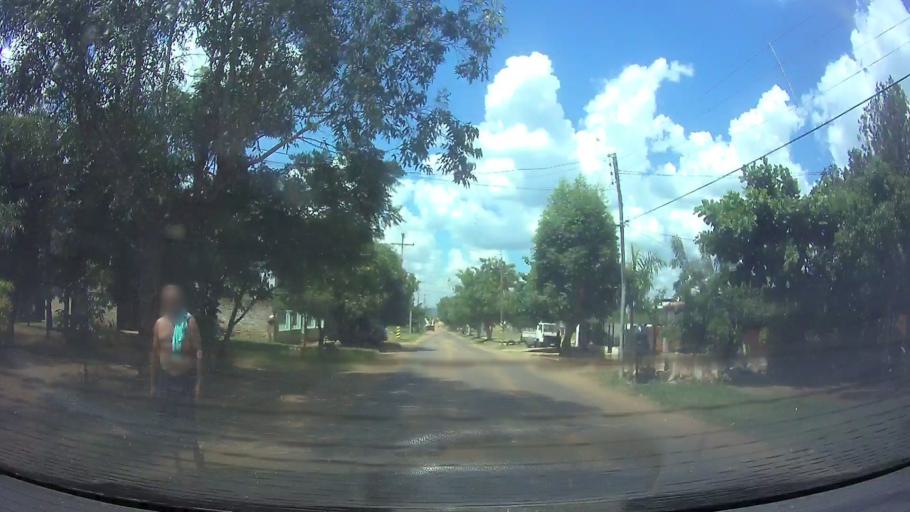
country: PY
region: Central
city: Limpio
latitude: -25.1655
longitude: -57.4271
